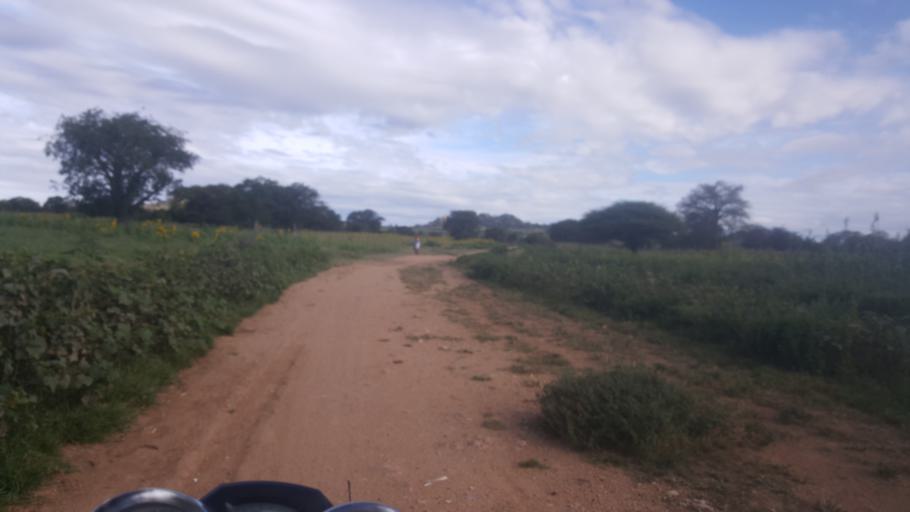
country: TZ
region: Dodoma
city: Dodoma
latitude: -6.0863
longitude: 35.5220
